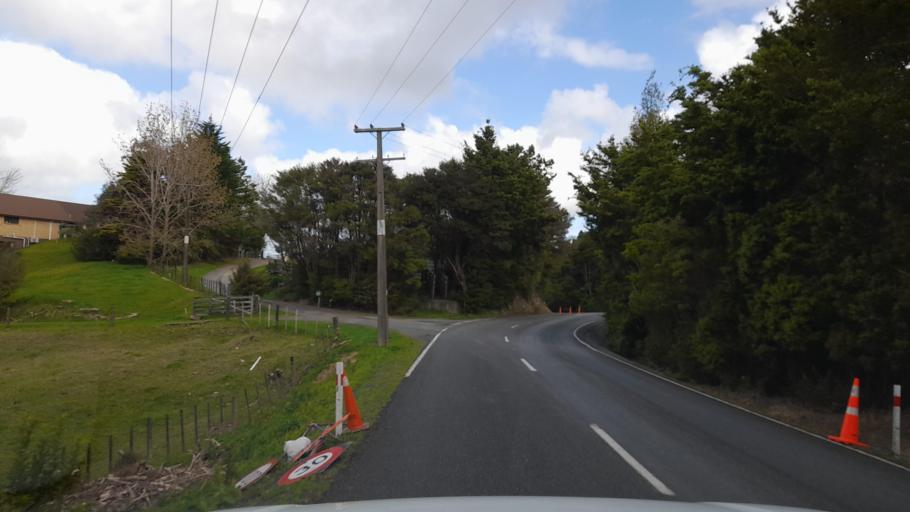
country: NZ
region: Northland
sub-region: Whangarei
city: Maungatapere
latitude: -35.7625
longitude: 174.2410
